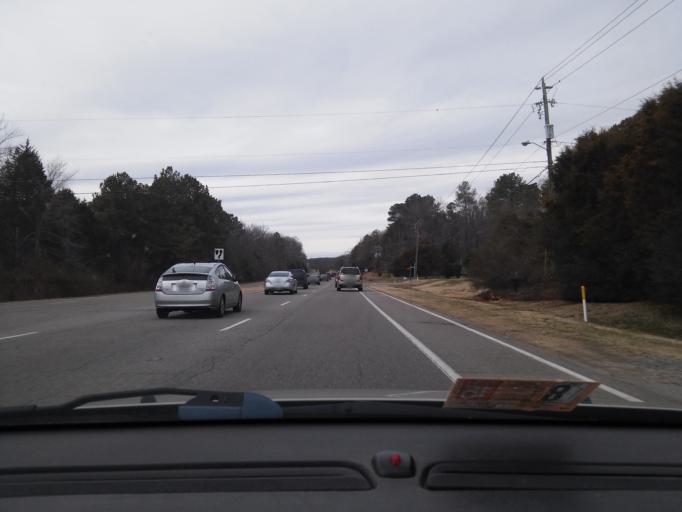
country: US
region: Virginia
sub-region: Chesterfield County
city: Bon Air
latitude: 37.5292
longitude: -77.6280
